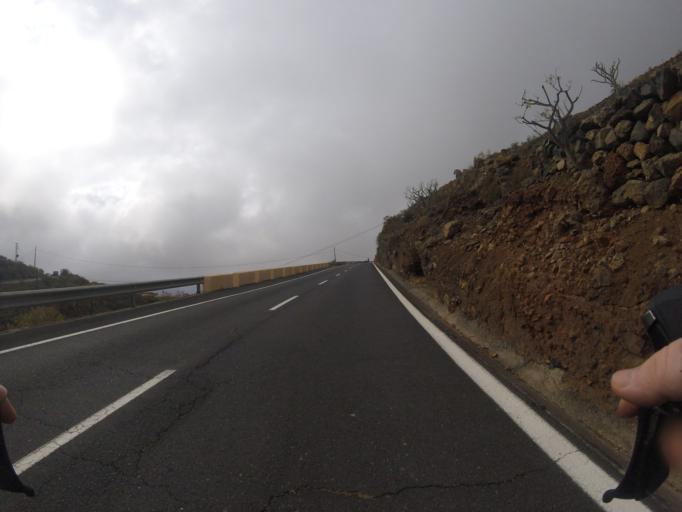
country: ES
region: Canary Islands
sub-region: Provincia de Santa Cruz de Tenerife
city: Fasnia
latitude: 28.2273
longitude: -16.4475
